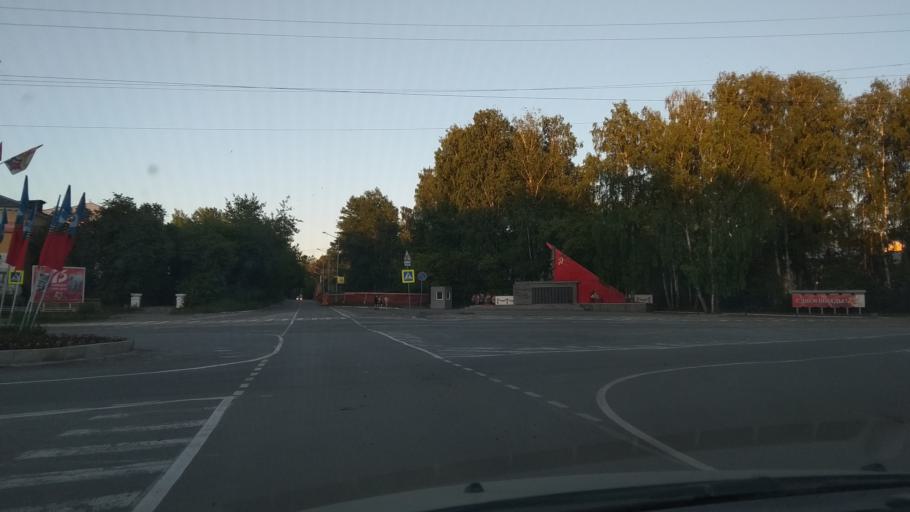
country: RU
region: Sverdlovsk
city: Sredneuralsk
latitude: 56.9888
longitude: 60.4630
